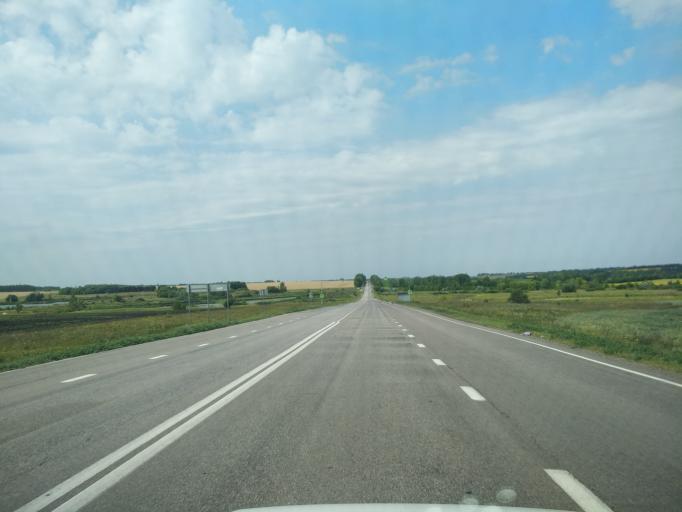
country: RU
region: Voronezj
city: Verkhnyaya Khava
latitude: 51.7028
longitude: 39.9746
